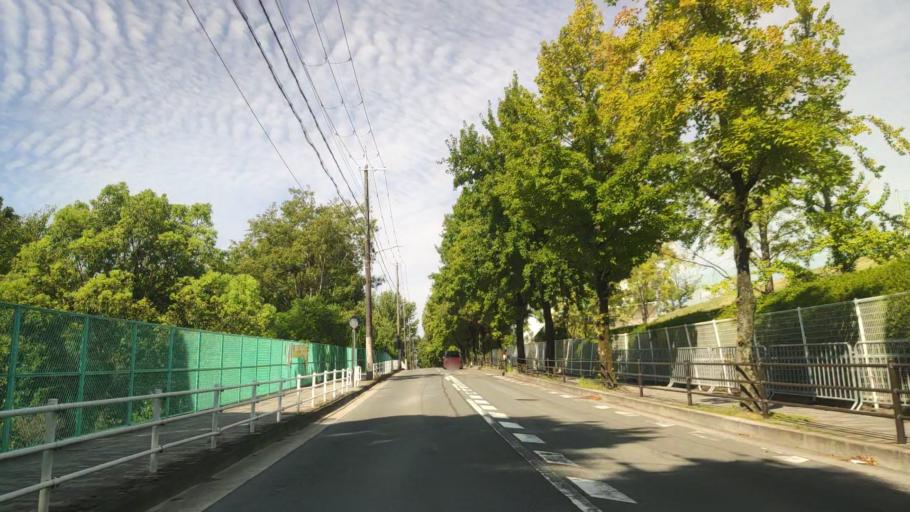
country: JP
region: Osaka
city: Mino
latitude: 34.8252
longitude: 135.5172
